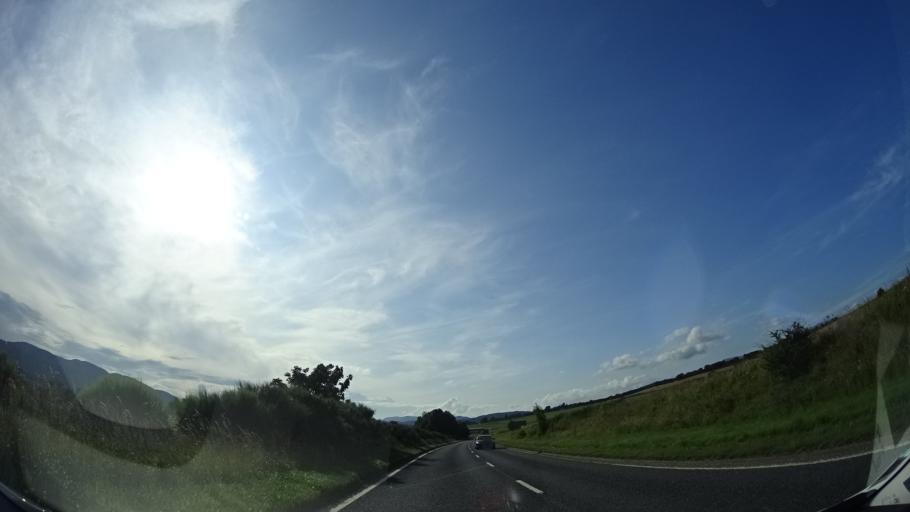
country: GB
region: Scotland
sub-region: Highland
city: Muir of Ord
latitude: 57.5585
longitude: -4.5456
